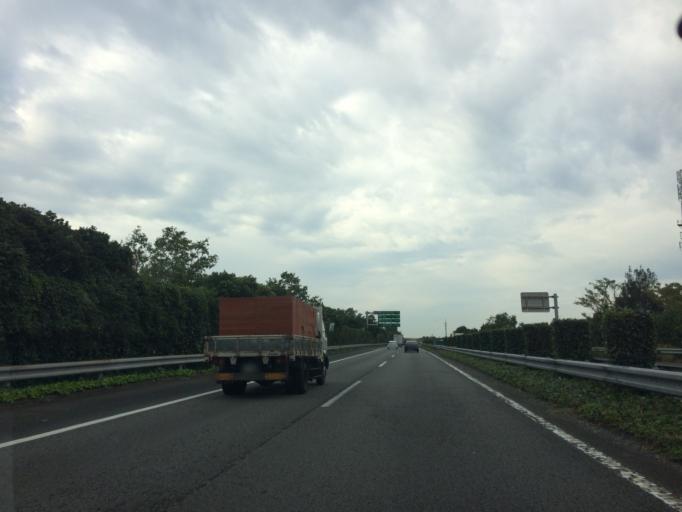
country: JP
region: Shizuoka
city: Yaizu
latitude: 34.8767
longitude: 138.2955
